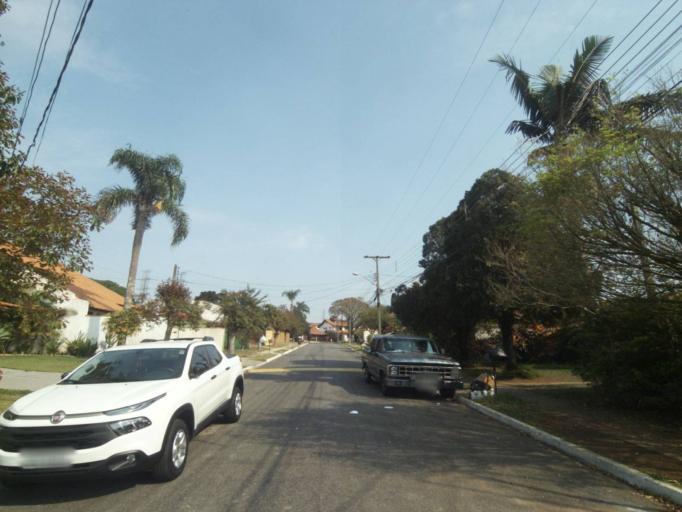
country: BR
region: Parana
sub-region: Pinhais
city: Pinhais
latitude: -25.4814
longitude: -49.2059
